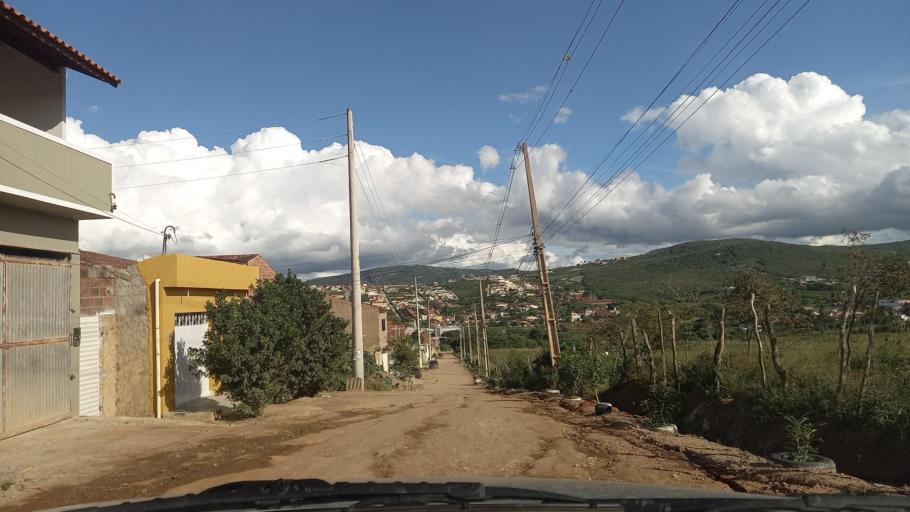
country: BR
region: Pernambuco
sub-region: Gravata
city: Gravata
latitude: -8.1990
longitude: -35.5824
